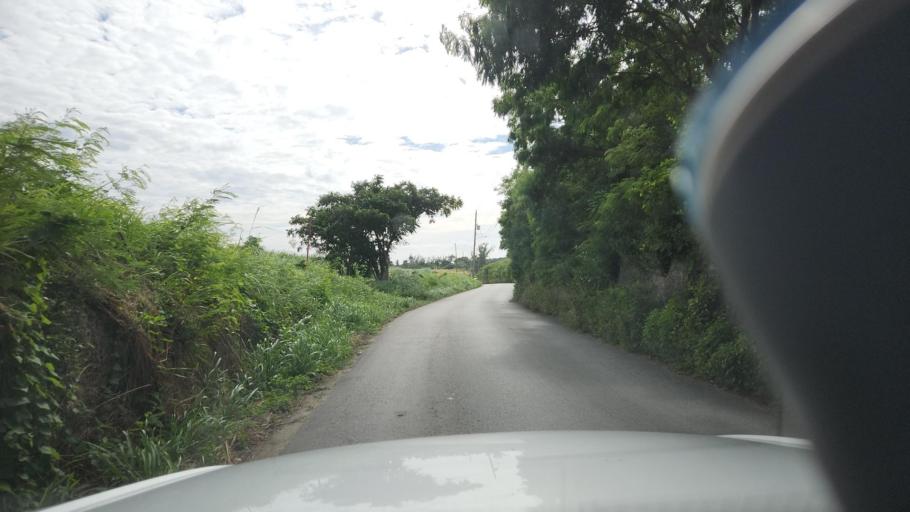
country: BB
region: Saint Lucy
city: Checker Hall
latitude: 13.2785
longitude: -59.6363
